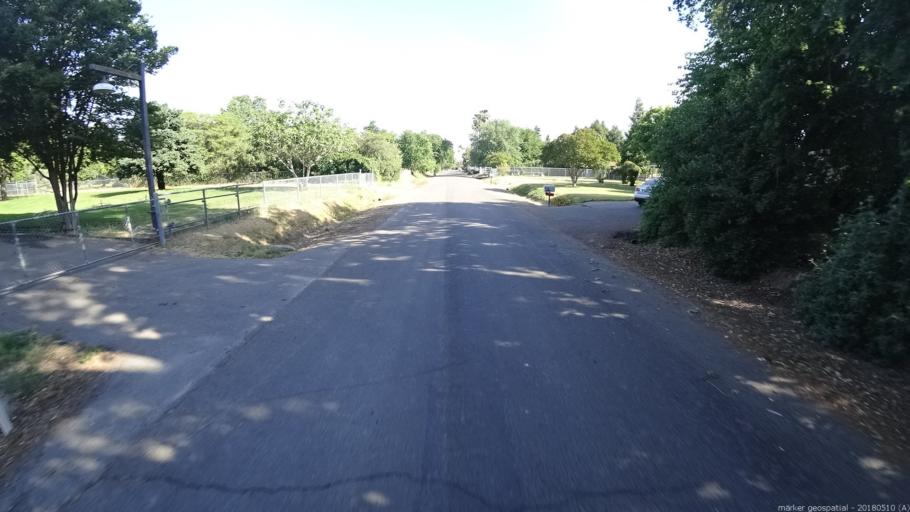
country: US
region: California
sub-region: Sacramento County
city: Rio Linda
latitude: 38.6603
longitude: -121.4784
